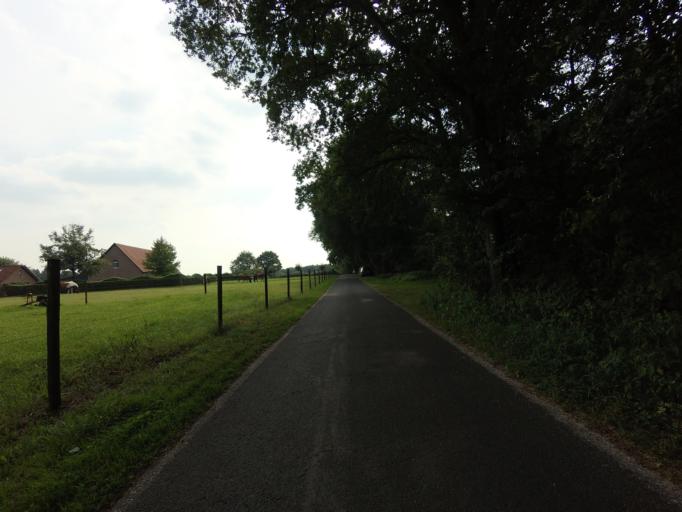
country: NL
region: Gelderland
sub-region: Gemeente Montferland
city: s-Heerenberg
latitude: 51.8800
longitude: 6.1793
